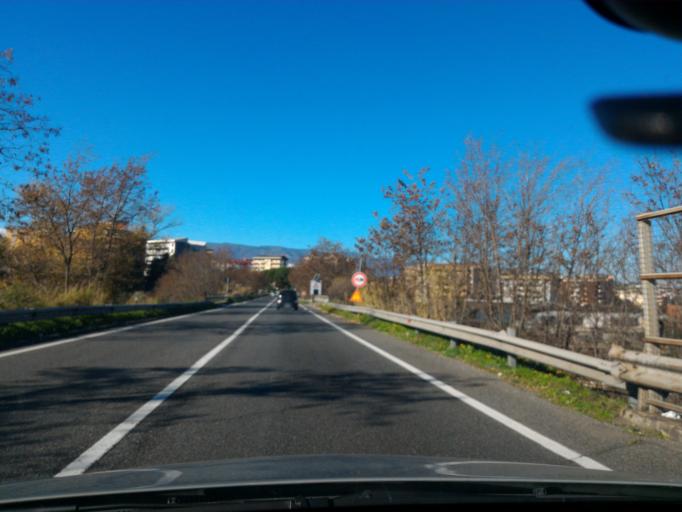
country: IT
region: Calabria
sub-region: Provincia di Cosenza
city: Quattromiglia
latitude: 39.3289
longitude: 16.2499
